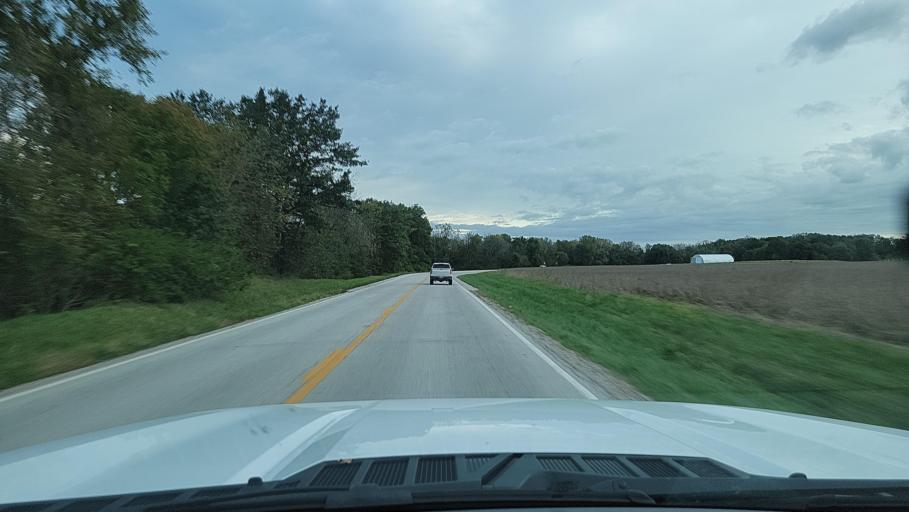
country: US
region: Illinois
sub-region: Schuyler County
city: Rushville
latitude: 40.1506
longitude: -90.5559
